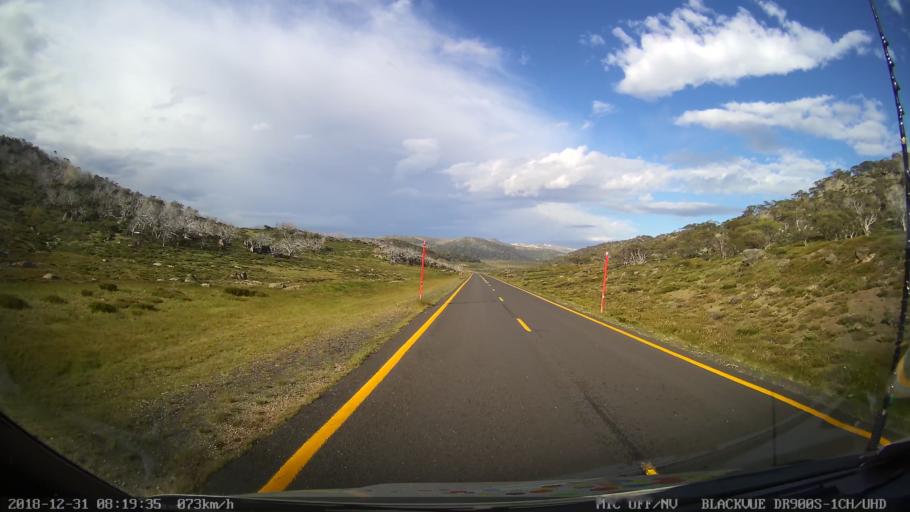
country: AU
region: New South Wales
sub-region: Snowy River
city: Jindabyne
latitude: -36.4201
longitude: 148.3840
